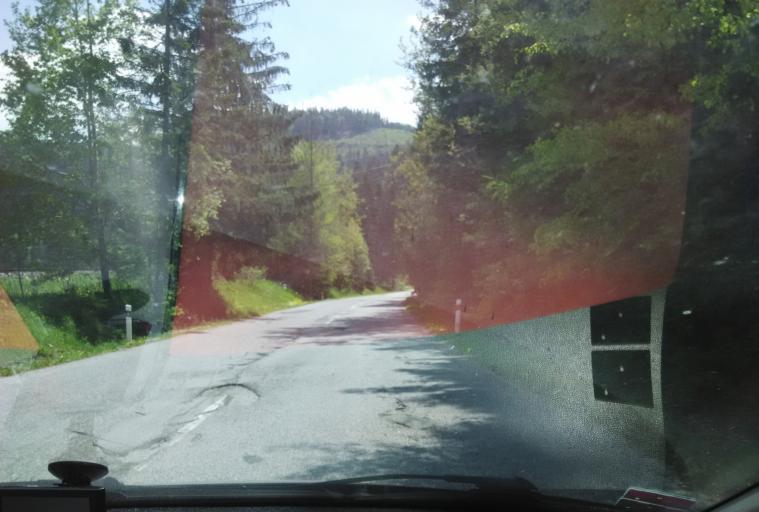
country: SK
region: Kosicky
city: Dobsina
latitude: 48.8548
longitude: 20.3825
